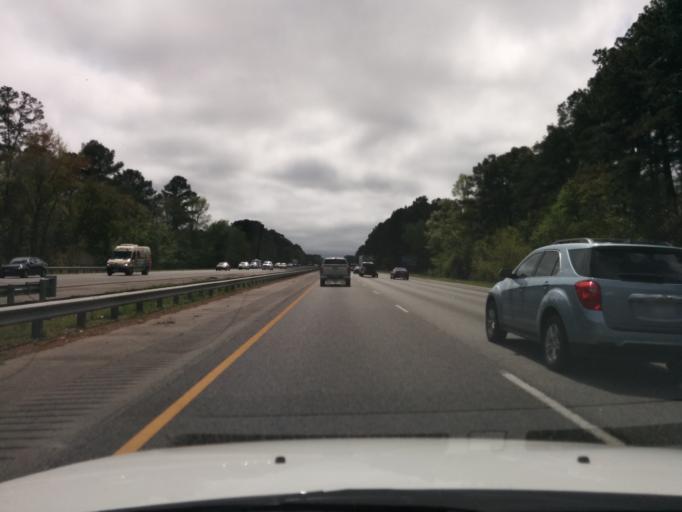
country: US
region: Georgia
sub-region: Chatham County
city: Georgetown
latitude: 32.0278
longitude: -81.2695
